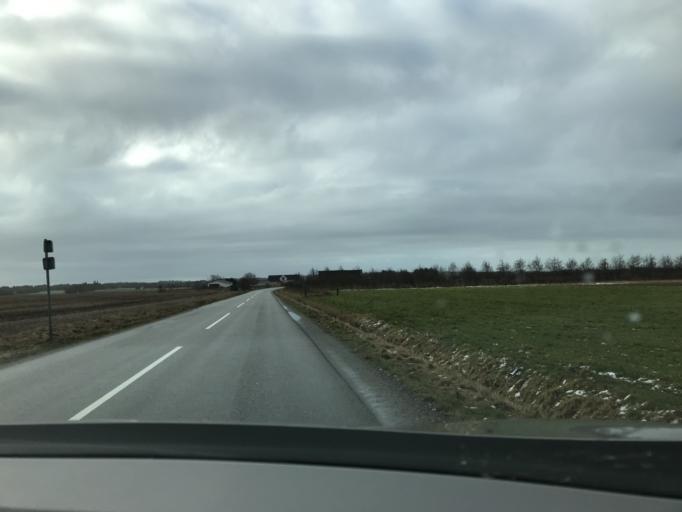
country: DK
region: South Denmark
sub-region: Varde Kommune
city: Oksbol
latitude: 55.7792
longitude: 8.2761
